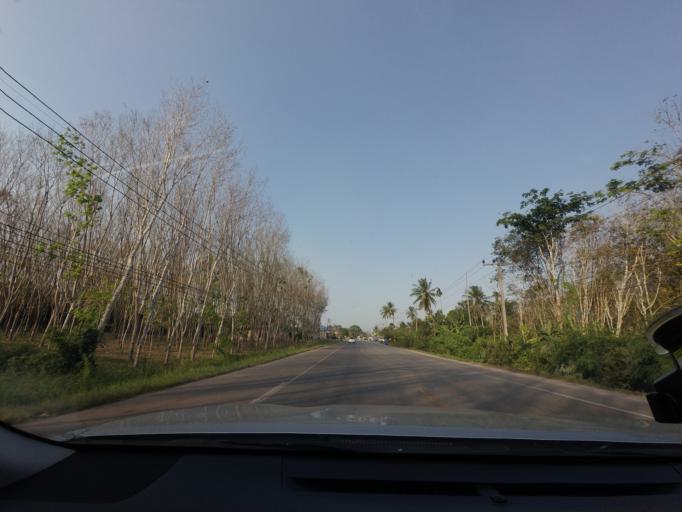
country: TH
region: Surat Thani
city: Phrasaeng
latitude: 8.5788
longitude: 99.2782
